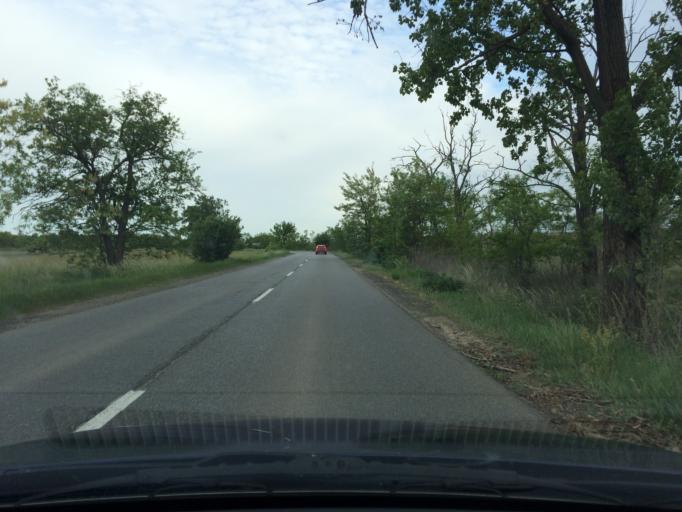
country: HU
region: Szabolcs-Szatmar-Bereg
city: Tiszavasvari
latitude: 47.9236
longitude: 21.3900
